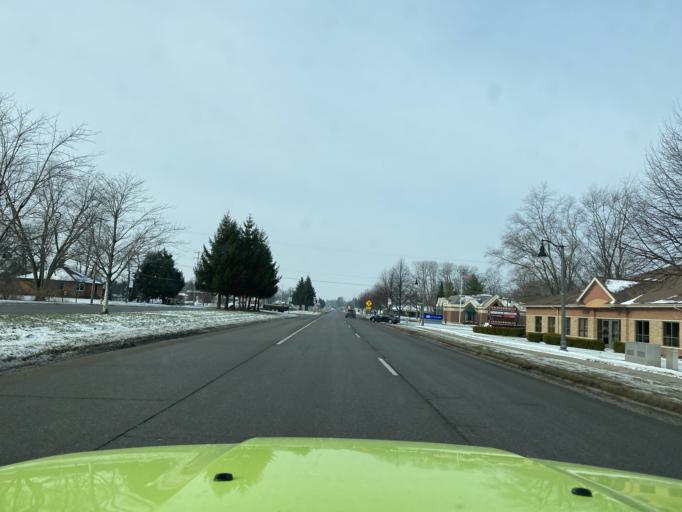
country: US
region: Michigan
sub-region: Ottawa County
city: Allendale
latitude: 42.9724
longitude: -85.9401
